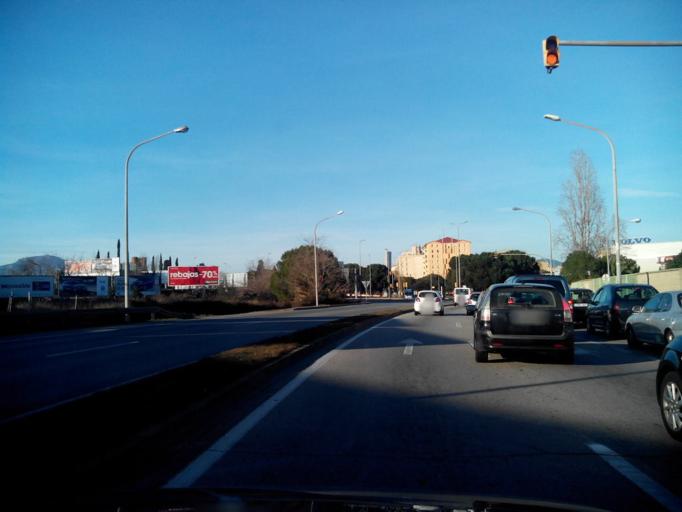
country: ES
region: Catalonia
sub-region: Provincia de Barcelona
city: Sant Quirze del Valles
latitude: 41.5353
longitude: 2.0957
